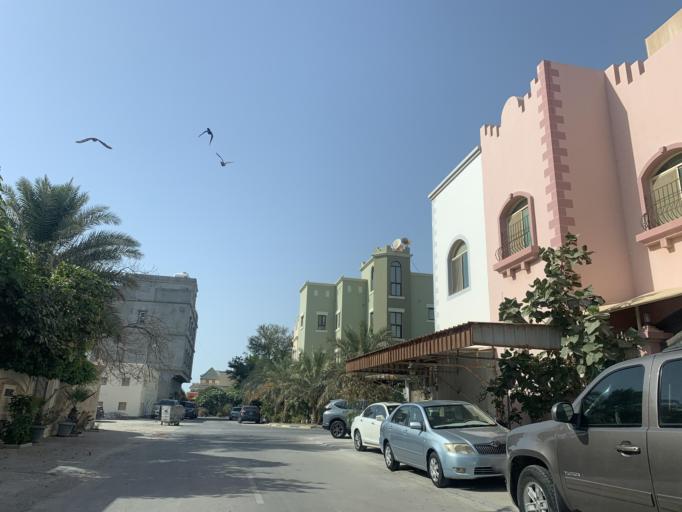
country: BH
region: Manama
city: Jidd Hafs
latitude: 26.2328
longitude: 50.4805
